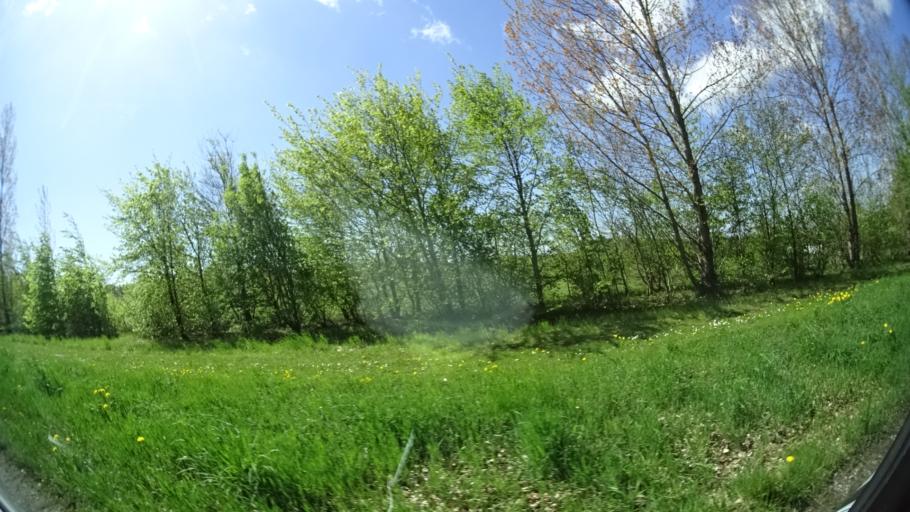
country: DK
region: Central Jutland
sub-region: Arhus Kommune
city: Framlev
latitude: 56.1213
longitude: 10.0167
